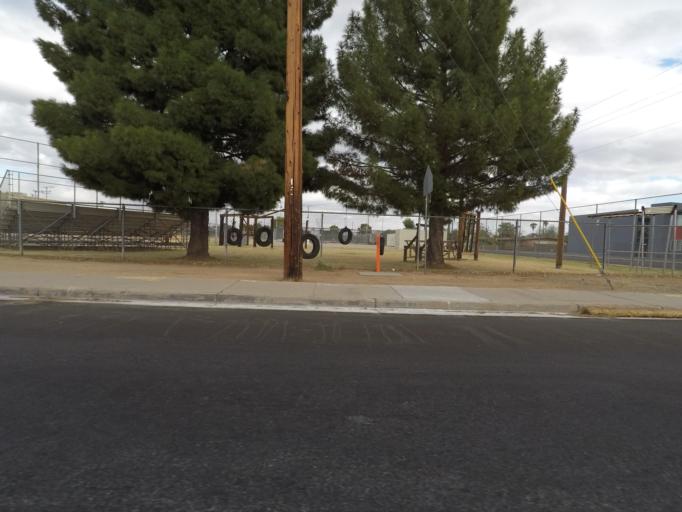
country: US
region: Arizona
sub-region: Maricopa County
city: Glendale
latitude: 33.5060
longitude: -112.1429
